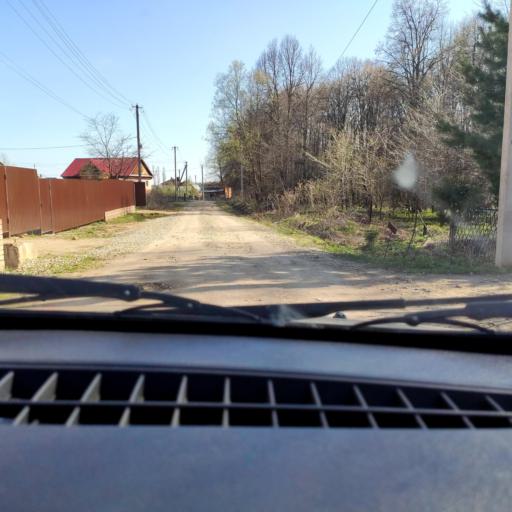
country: RU
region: Bashkortostan
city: Kabakovo
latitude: 54.5949
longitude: 56.1739
